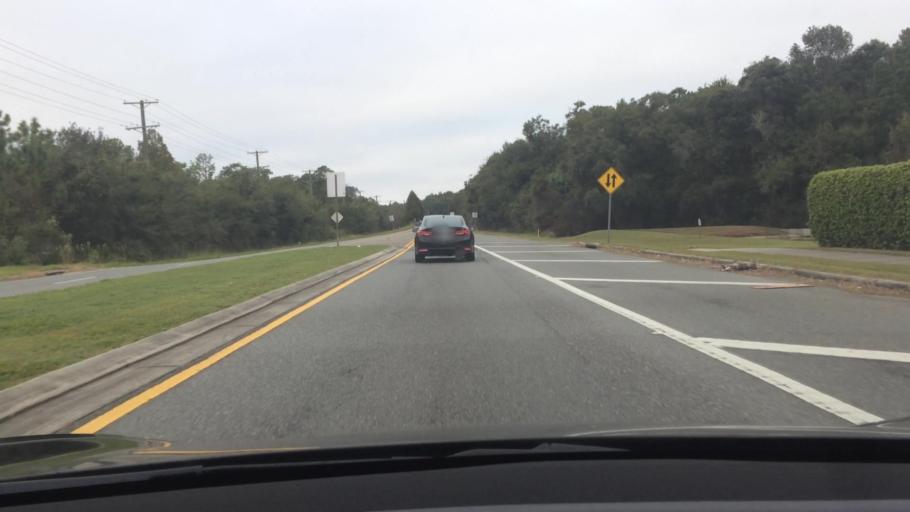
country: US
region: Florida
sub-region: Hillsborough County
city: Pebble Creek
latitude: 28.1713
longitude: -82.3589
